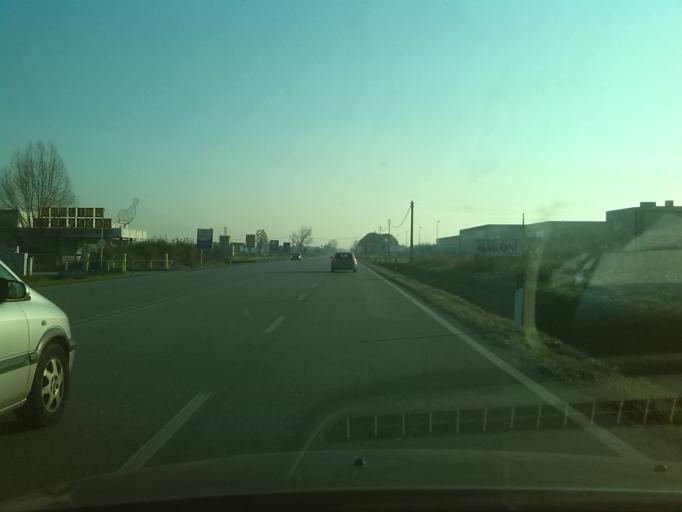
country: IT
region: Friuli Venezia Giulia
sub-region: Provincia di Udine
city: Pertegada
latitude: 45.7311
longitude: 13.0437
